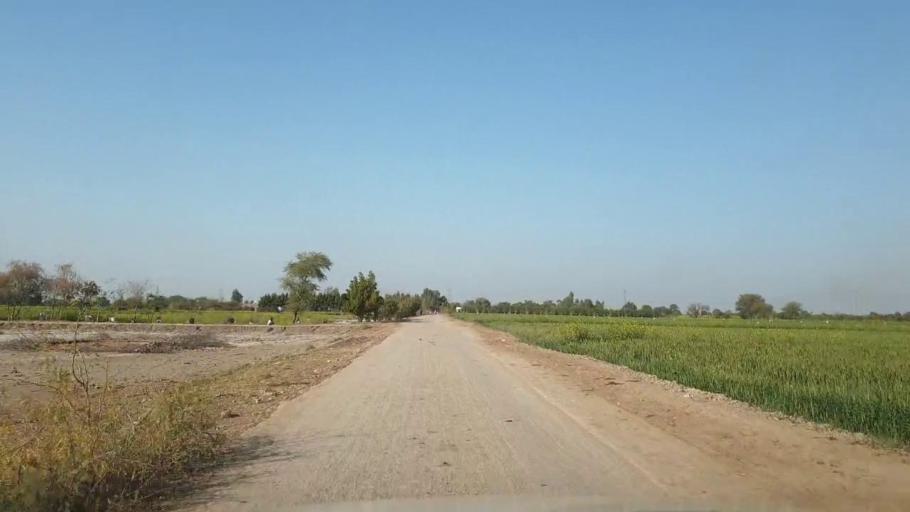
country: PK
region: Sindh
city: Tando Allahyar
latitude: 25.5090
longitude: 68.6550
